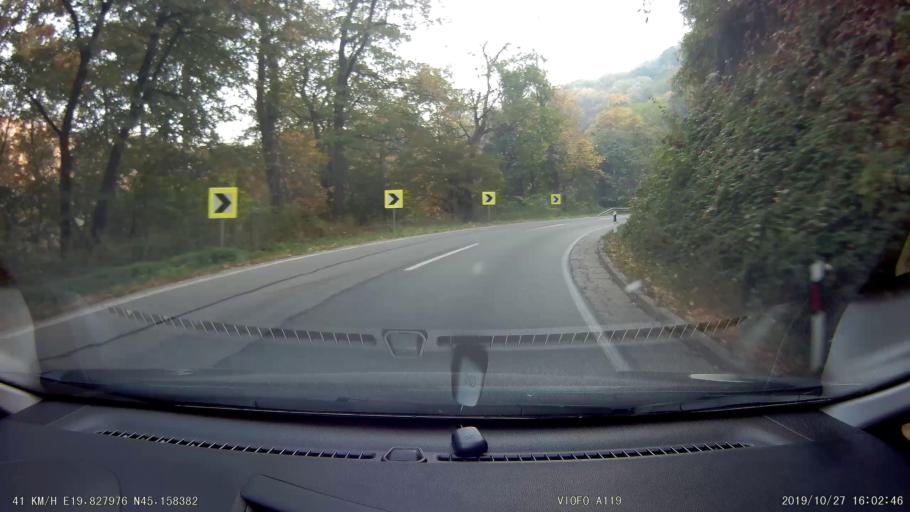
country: RS
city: Vrdnik
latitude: 45.1582
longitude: 19.8282
